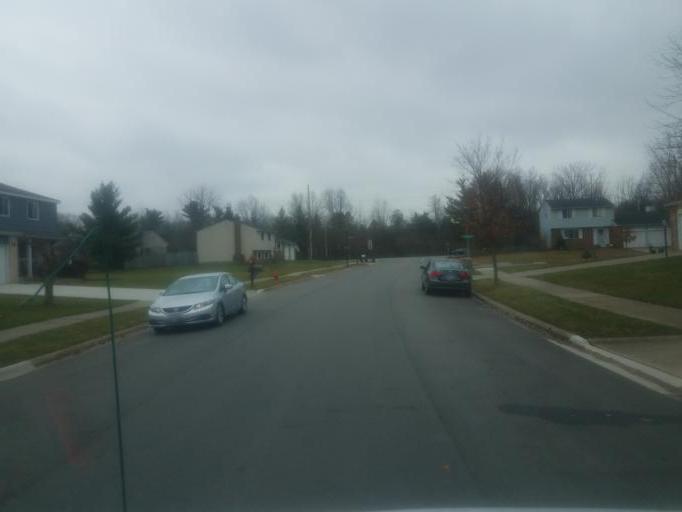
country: US
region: Ohio
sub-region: Franklin County
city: Westerville
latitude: 40.1266
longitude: -82.9681
